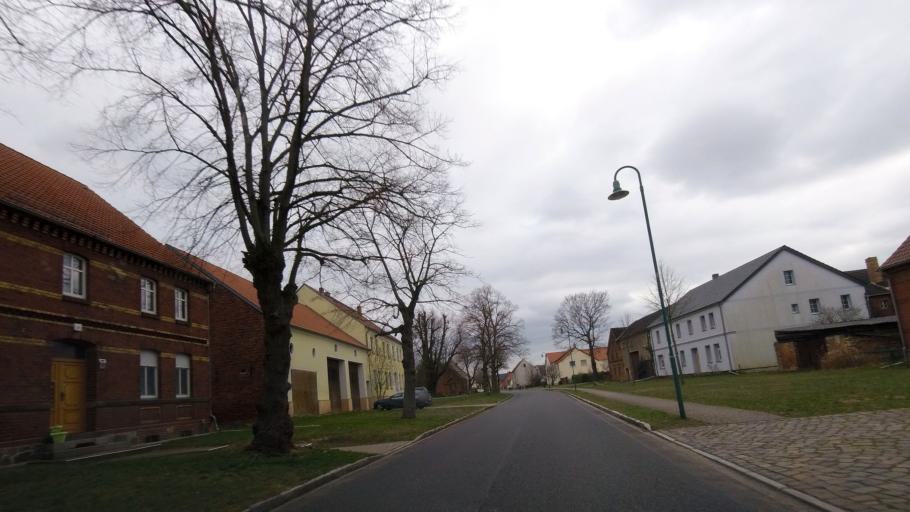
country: DE
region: Brandenburg
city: Niedergorsdorf
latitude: 51.9867
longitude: 12.9456
